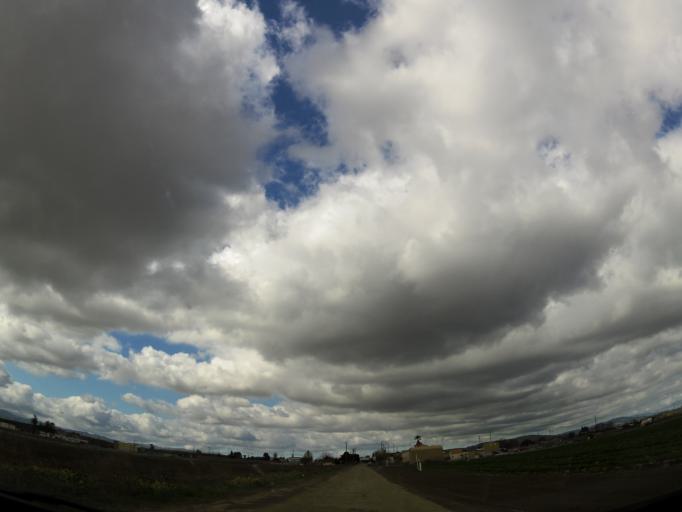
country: US
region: California
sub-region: San Benito County
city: Hollister
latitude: 36.8659
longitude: -121.3960
